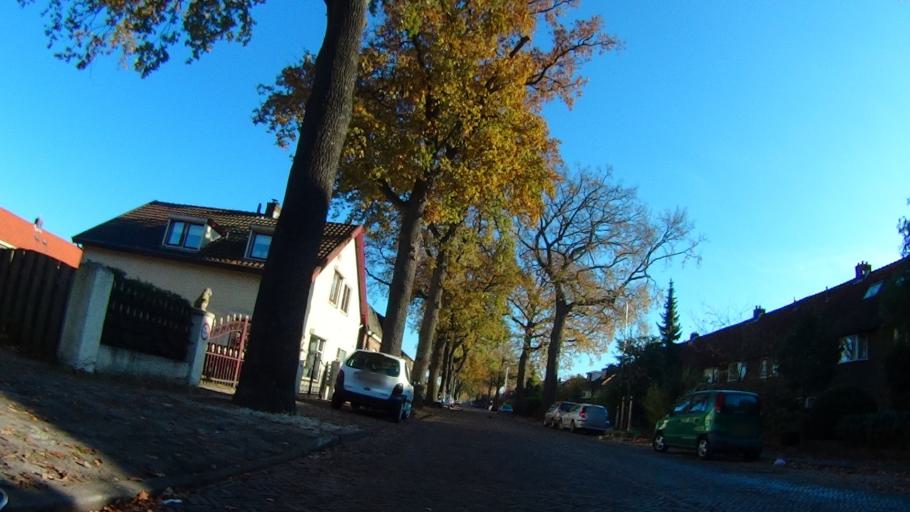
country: NL
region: Utrecht
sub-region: Gemeente Amersfoort
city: Hoogland
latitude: 52.1586
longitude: 5.3577
